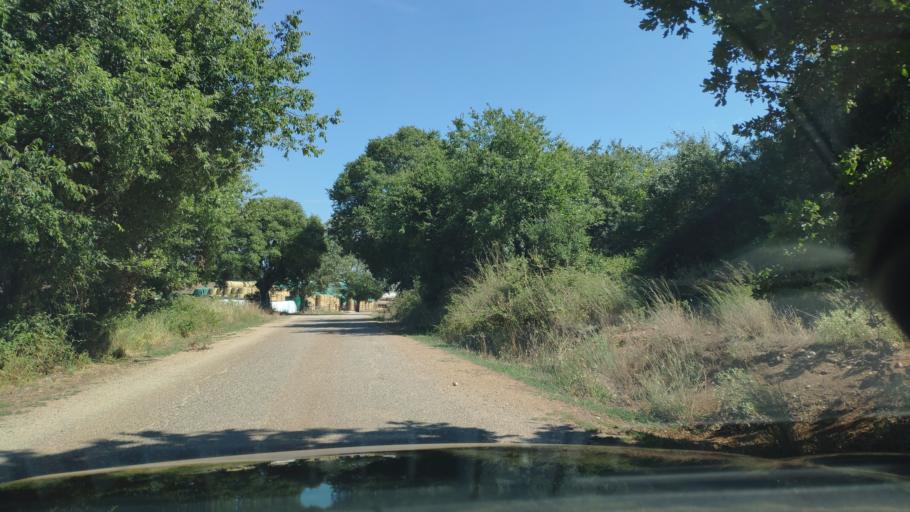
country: GR
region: West Greece
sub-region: Nomos Aitolias kai Akarnanias
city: Katouna
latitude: 38.8479
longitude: 21.0929
